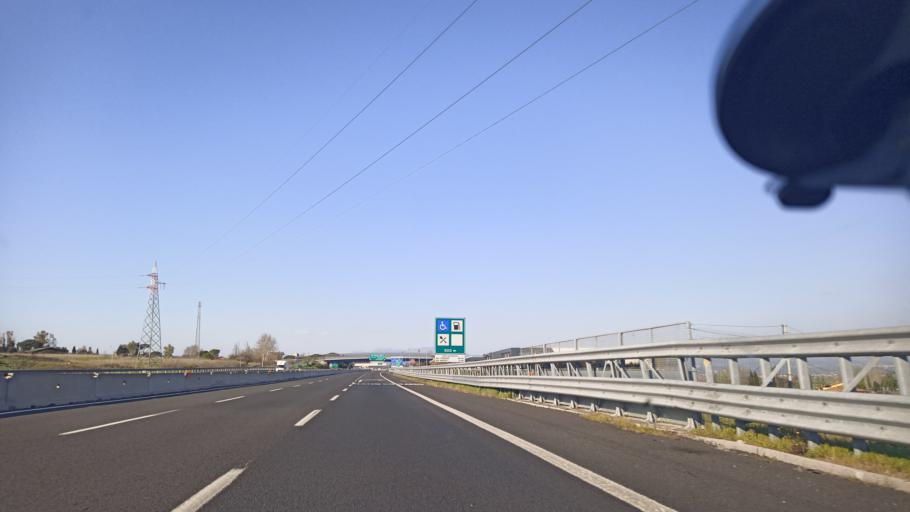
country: IT
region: Latium
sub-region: Citta metropolitana di Roma Capitale
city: Bivio di Capanelle
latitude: 42.1253
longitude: 12.5970
